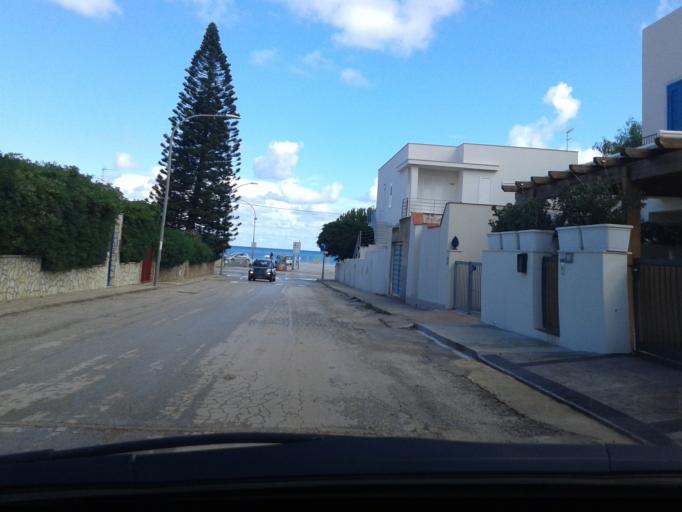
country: IT
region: Sicily
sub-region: Trapani
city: San Vito Lo Capo
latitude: 38.1741
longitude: 12.7424
